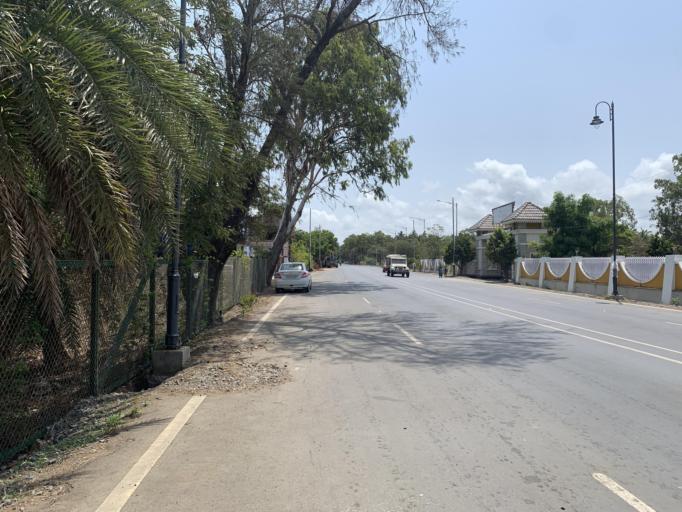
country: IN
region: Daman and Diu
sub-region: Daman District
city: Daman
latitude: 20.4589
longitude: 72.8452
